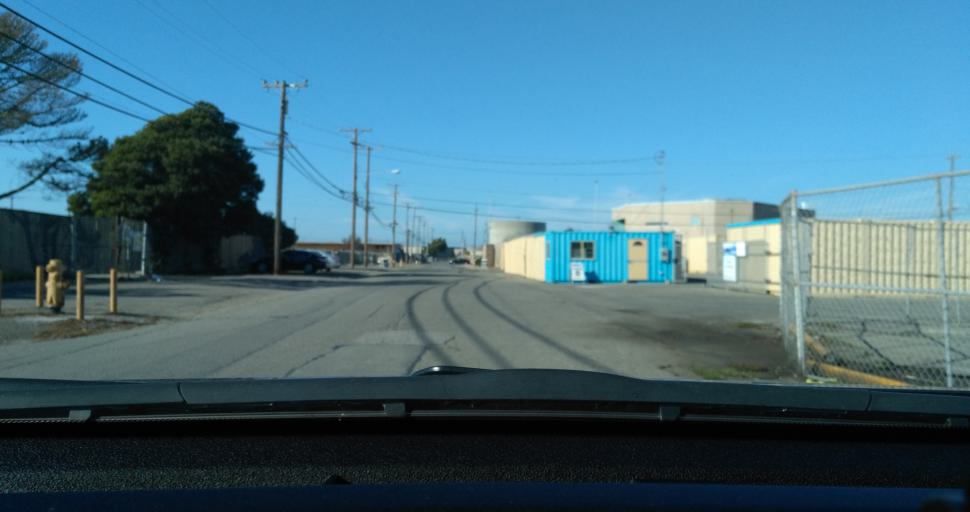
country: US
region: California
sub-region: San Francisco County
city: San Francisco
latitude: 37.8279
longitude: -122.3687
